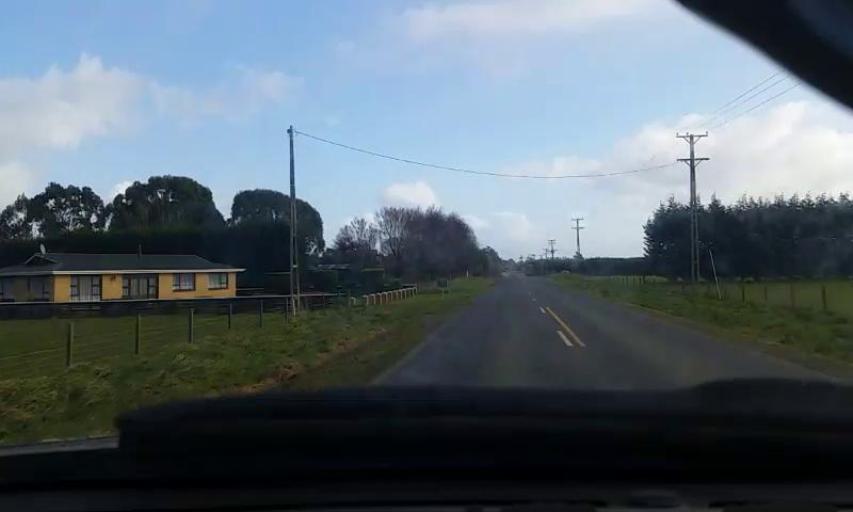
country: NZ
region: Southland
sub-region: Invercargill City
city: Invercargill
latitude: -46.3581
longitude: 168.3380
